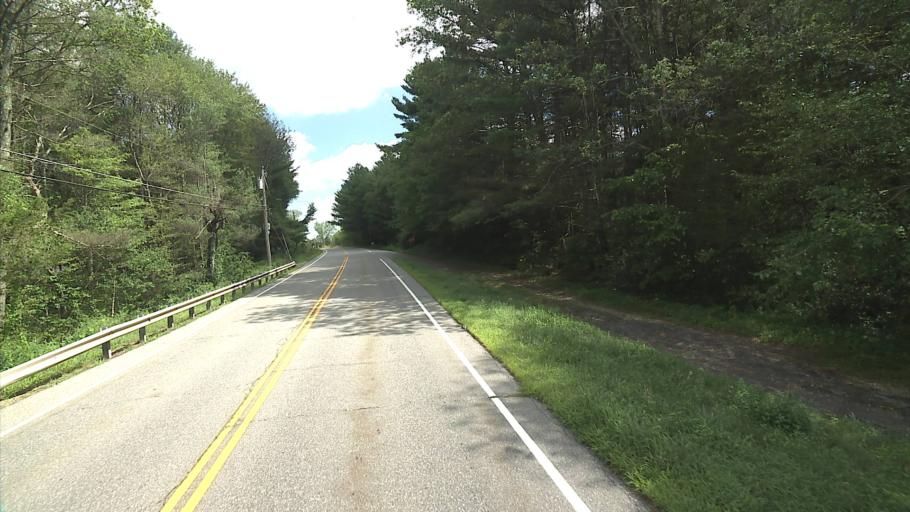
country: US
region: Connecticut
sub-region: Windham County
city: Windham
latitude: 41.8256
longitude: -72.1014
